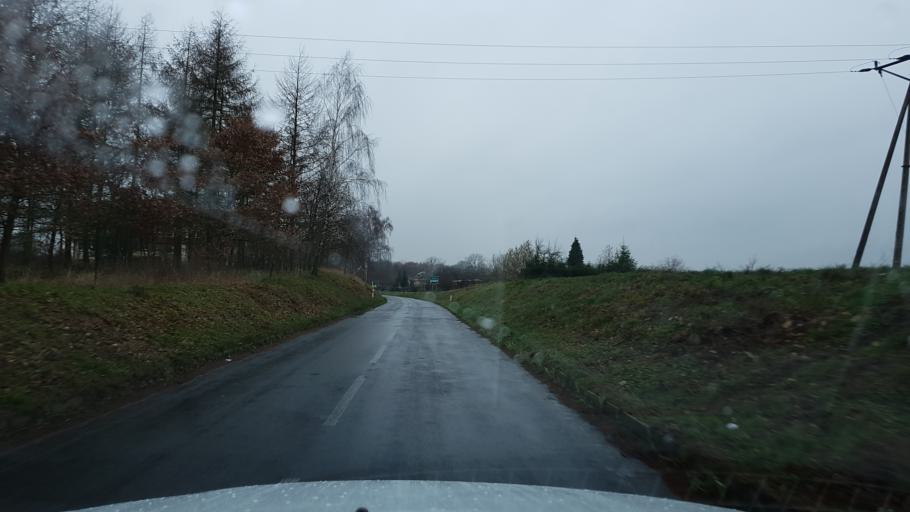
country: PL
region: West Pomeranian Voivodeship
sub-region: Powiat lobeski
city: Dobra
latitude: 53.5808
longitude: 15.3227
